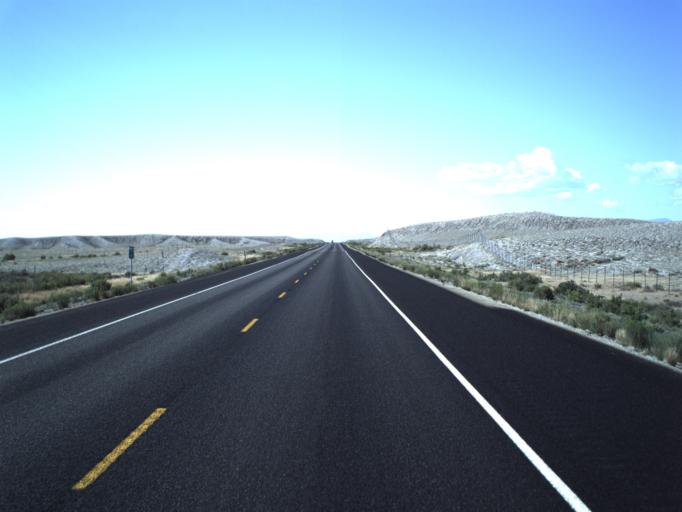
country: US
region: Utah
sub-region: Emery County
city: Ferron
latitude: 38.9894
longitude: -111.1693
